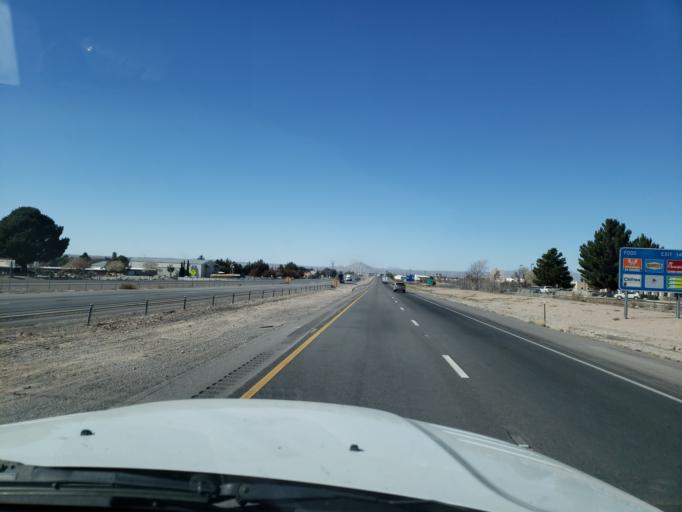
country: US
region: New Mexico
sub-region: Dona Ana County
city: University Park
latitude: 32.2735
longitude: -106.7542
